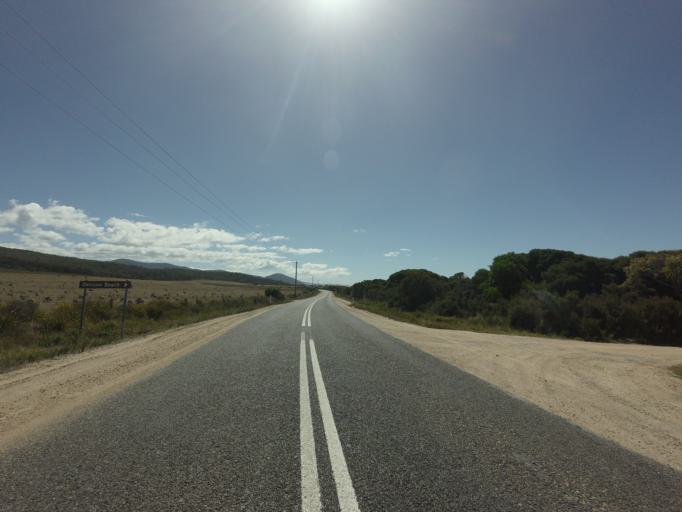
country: AU
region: Tasmania
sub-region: Break O'Day
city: St Helens
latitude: -41.8067
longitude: 148.2627
